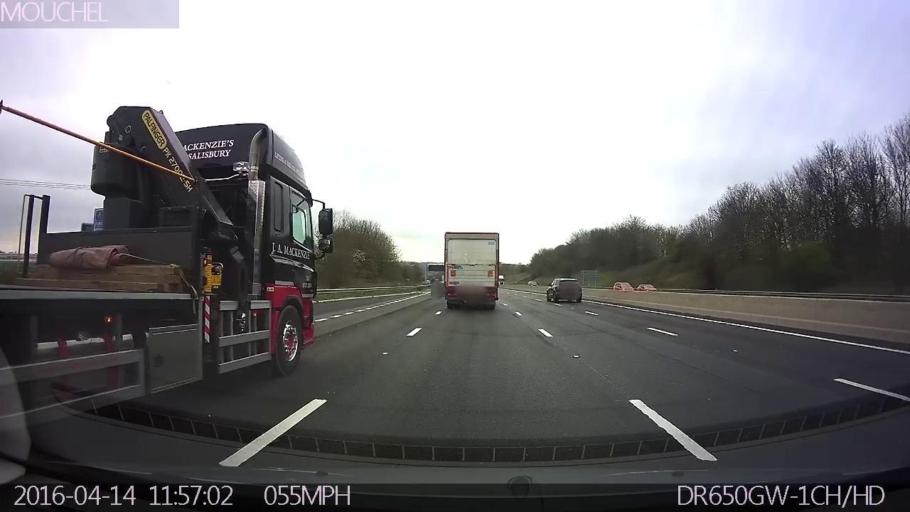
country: GB
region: England
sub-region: Derbyshire
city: Blackwell
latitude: 53.1225
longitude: -1.3322
